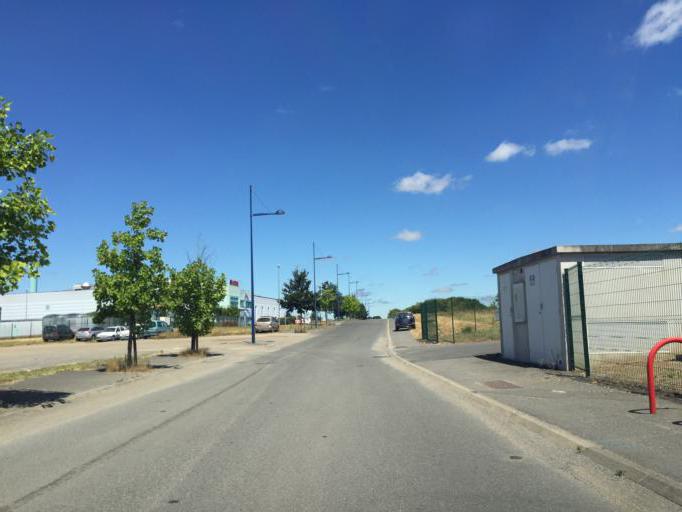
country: FR
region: Auvergne
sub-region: Departement de l'Allier
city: Avermes
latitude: 46.5938
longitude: 3.3289
